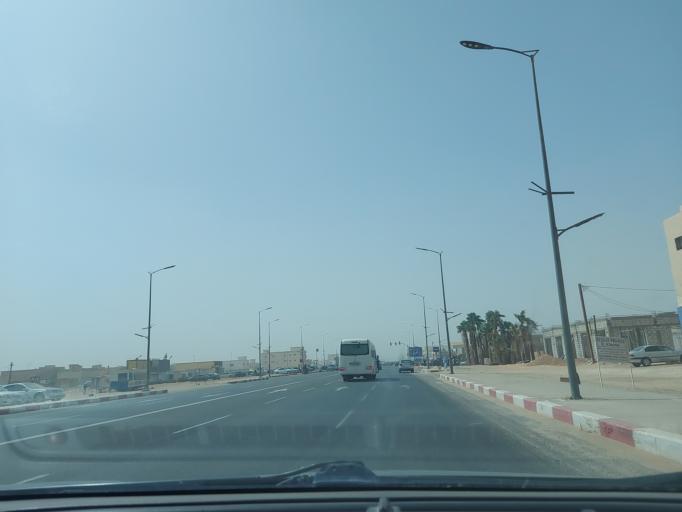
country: MR
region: Nouakchott
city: Nouakchott
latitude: 18.1288
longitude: -16.0032
